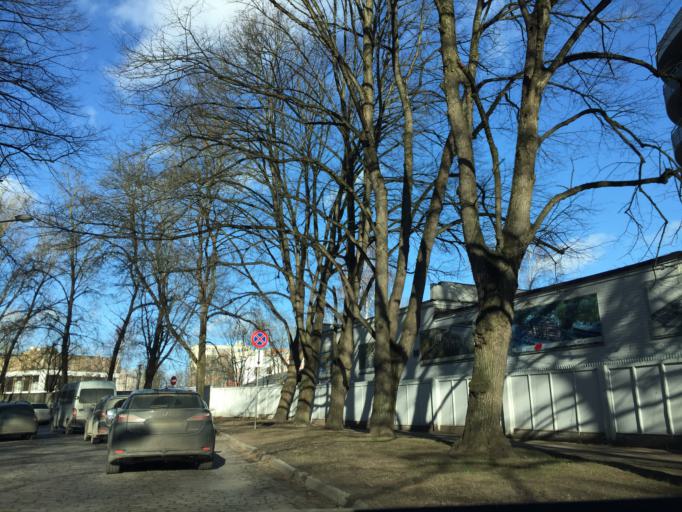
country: LV
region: Riga
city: Riga
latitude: 56.9737
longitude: 24.1475
